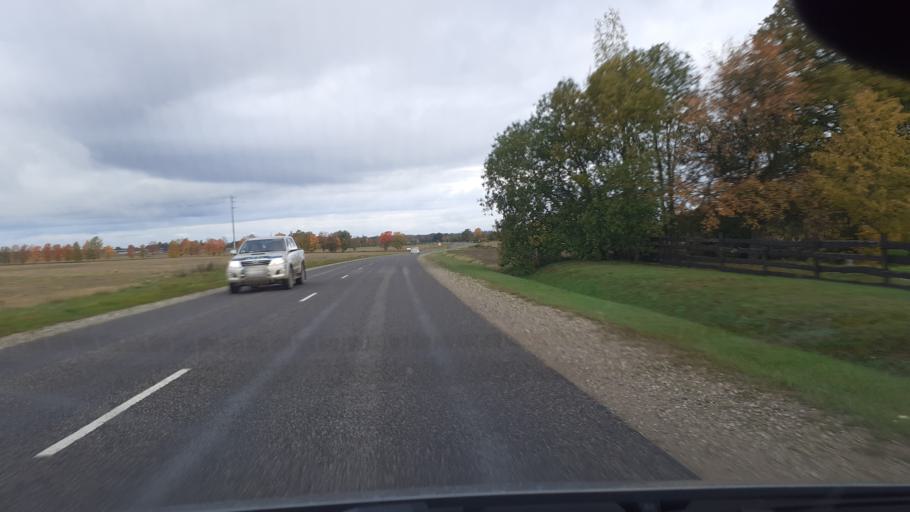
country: LV
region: Kuldigas Rajons
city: Kuldiga
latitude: 56.9992
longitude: 21.8990
